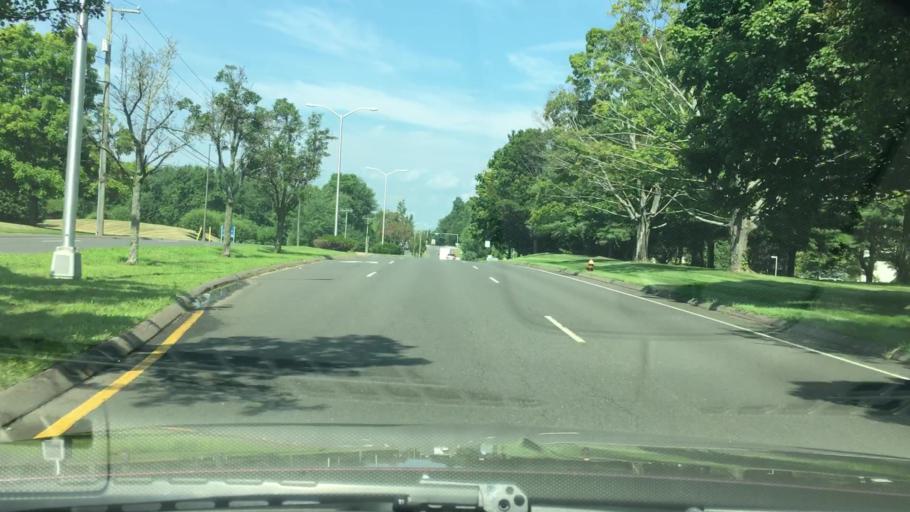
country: US
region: Connecticut
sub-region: Hartford County
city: Windsor
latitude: 41.8725
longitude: -72.6751
